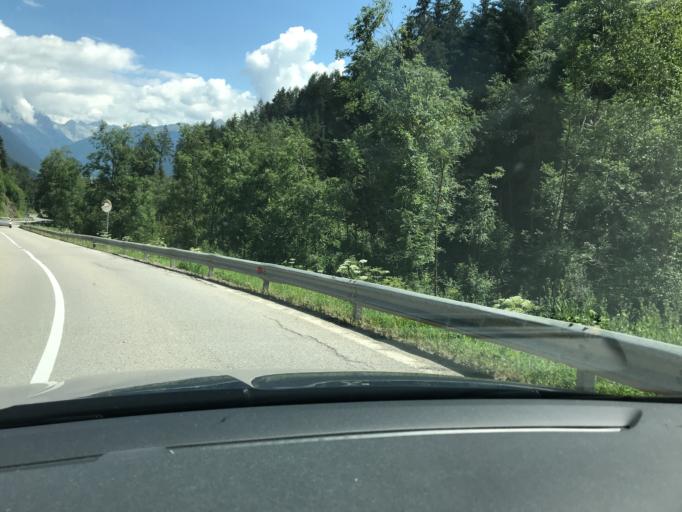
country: IT
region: Trentino-Alto Adige
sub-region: Bolzano
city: Valdaora di Mezzo
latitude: 46.7486
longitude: 12.0129
